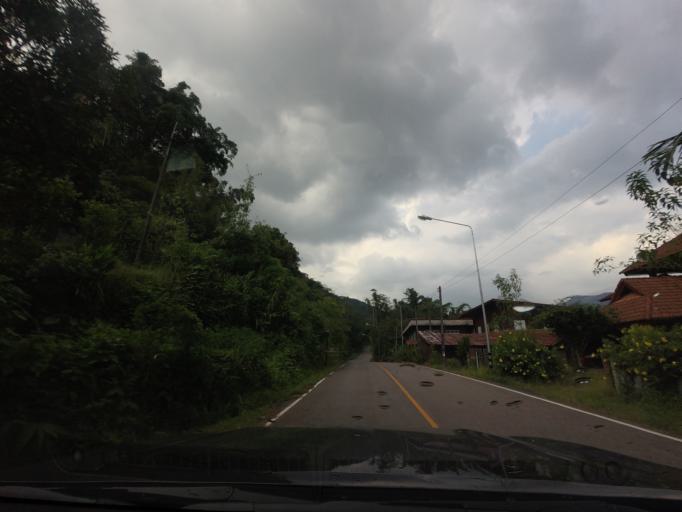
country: TH
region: Nan
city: Bo Kluea
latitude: 19.2795
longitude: 101.1759
